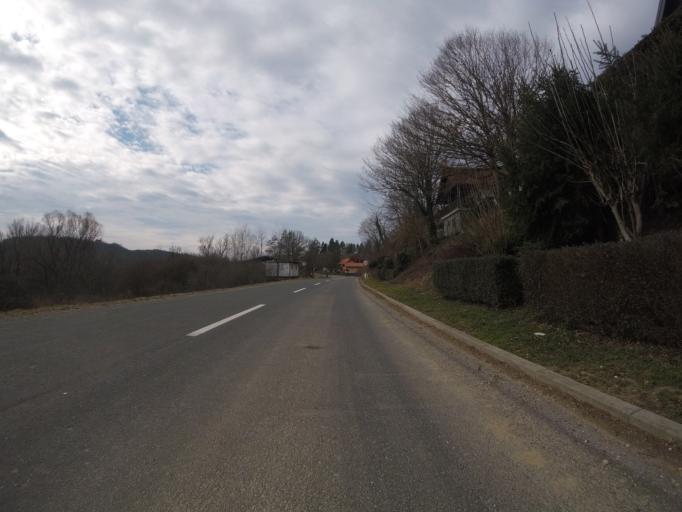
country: HR
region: Sisacko-Moslavacka
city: Glina
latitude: 45.4869
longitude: 16.0071
